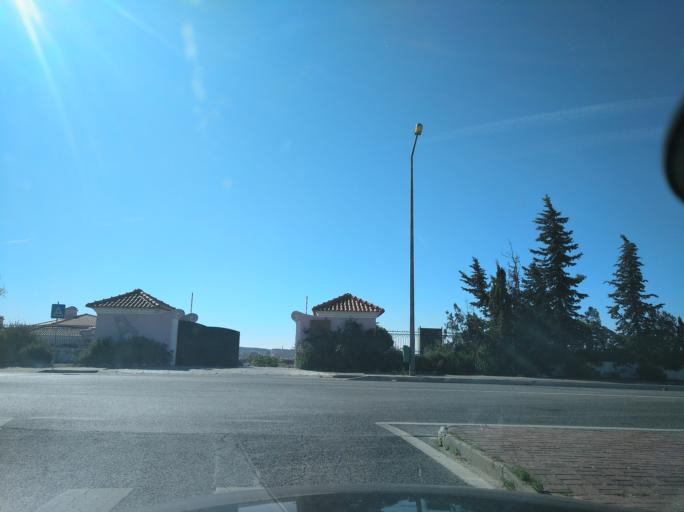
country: PT
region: Lisbon
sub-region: Loures
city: Moscavide
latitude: 38.7566
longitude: -9.1271
